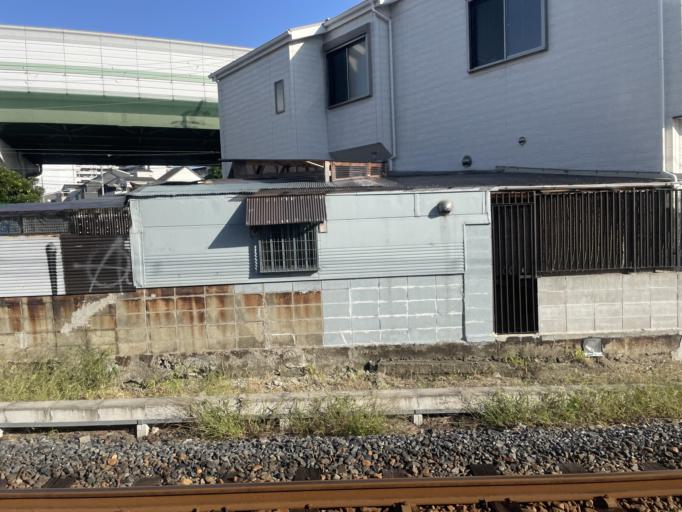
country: JP
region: Osaka
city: Osaka-shi
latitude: 34.6569
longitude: 135.4849
